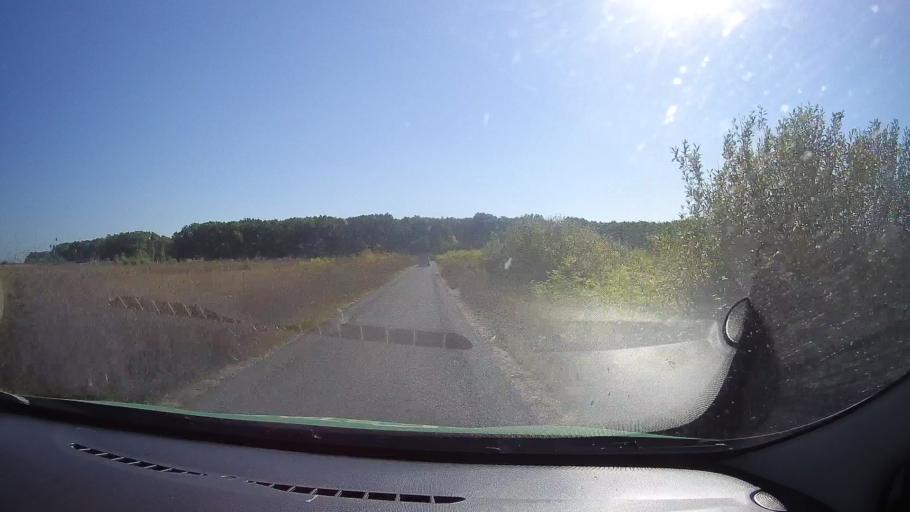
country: RO
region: Satu Mare
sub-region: Comuna Doba
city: Doba
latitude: 47.7196
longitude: 22.7274
